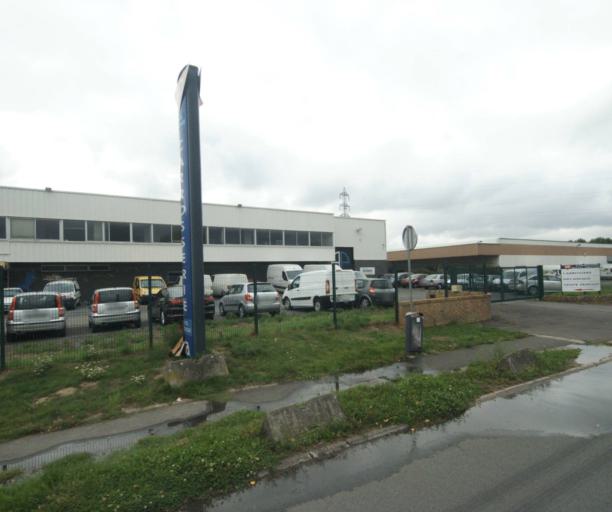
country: FR
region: Nord-Pas-de-Calais
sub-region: Departement du Nord
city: Lezennes
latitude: 50.6138
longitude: 3.1020
